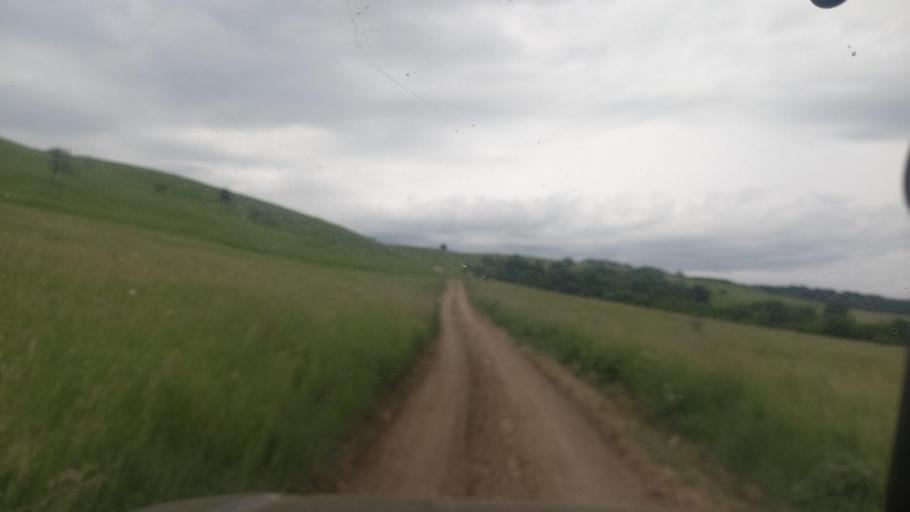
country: RU
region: Krasnodarskiy
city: Peredovaya
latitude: 44.0782
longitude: 41.3640
